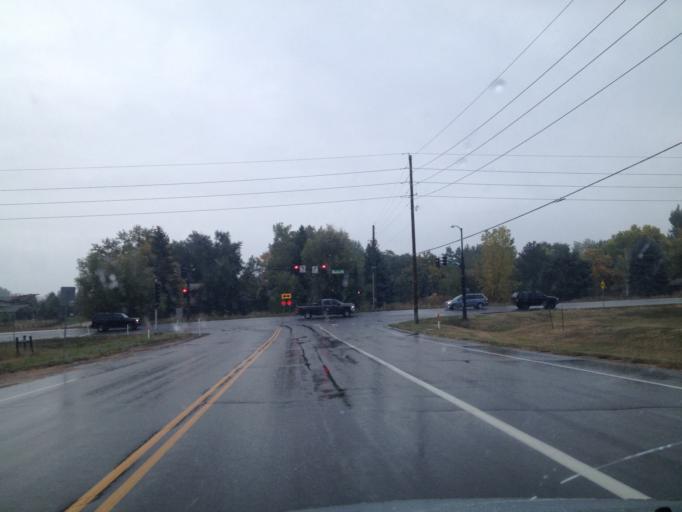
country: US
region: Colorado
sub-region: Boulder County
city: Superior
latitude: 39.9995
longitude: -105.1749
